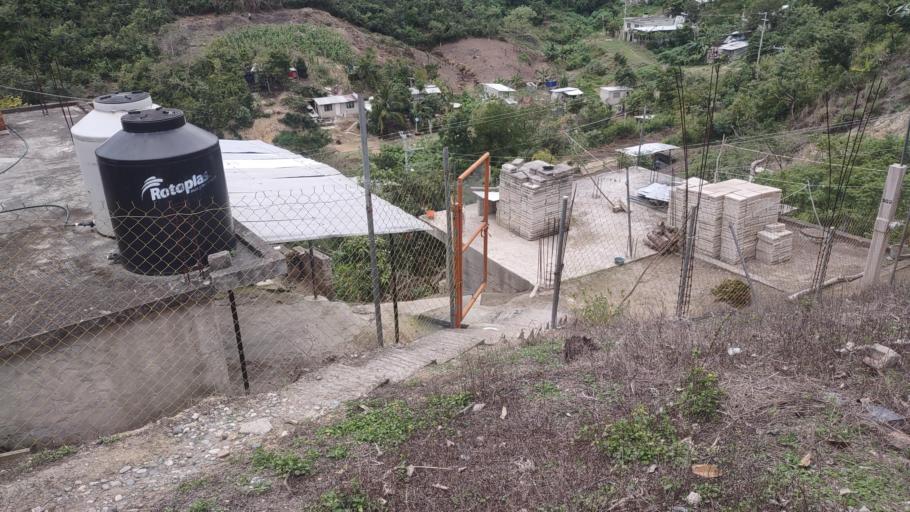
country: MX
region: Veracruz
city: Papantla de Olarte
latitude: 20.4335
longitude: -97.3393
